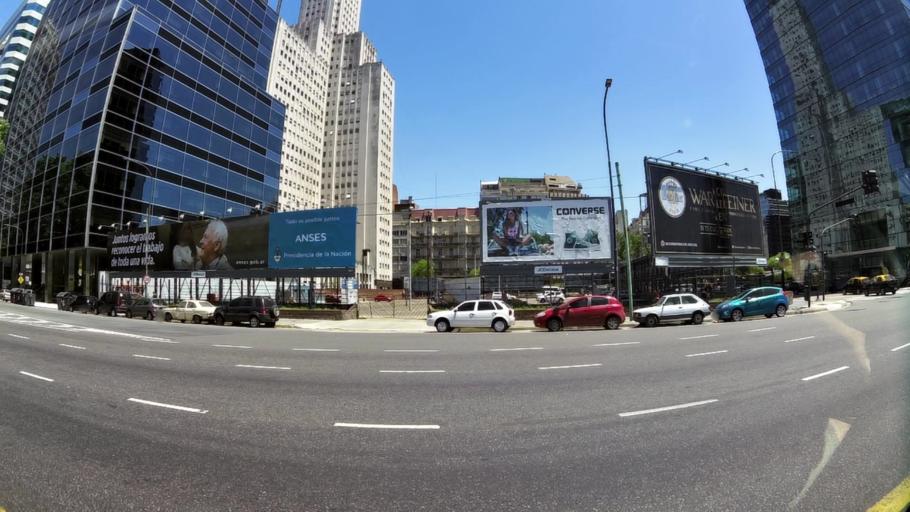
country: AR
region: Buenos Aires F.D.
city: Buenos Aires
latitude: -34.5985
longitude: -58.3695
